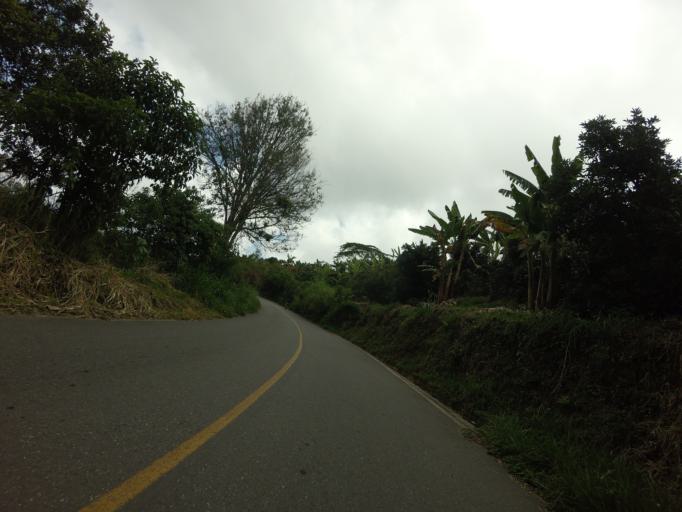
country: CO
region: Caldas
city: Marquetalia
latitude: 5.3054
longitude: -75.0106
